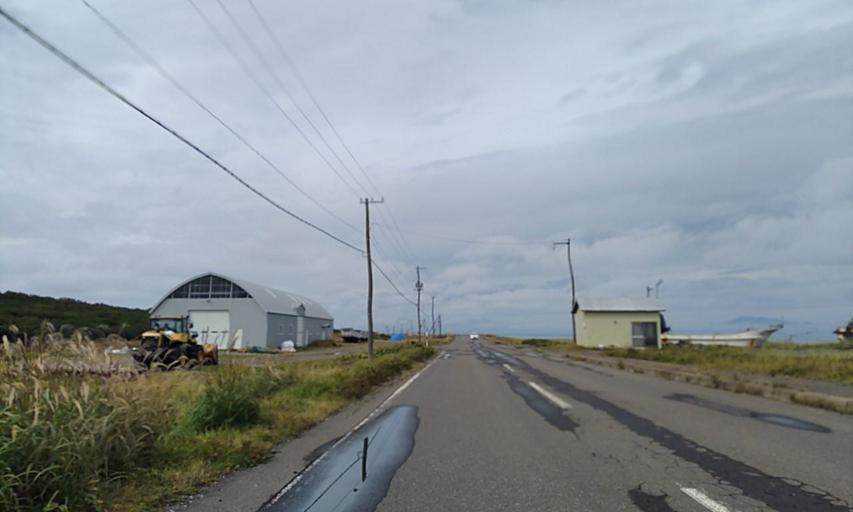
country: JP
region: Hokkaido
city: Shibetsu
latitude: 43.6068
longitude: 145.2865
